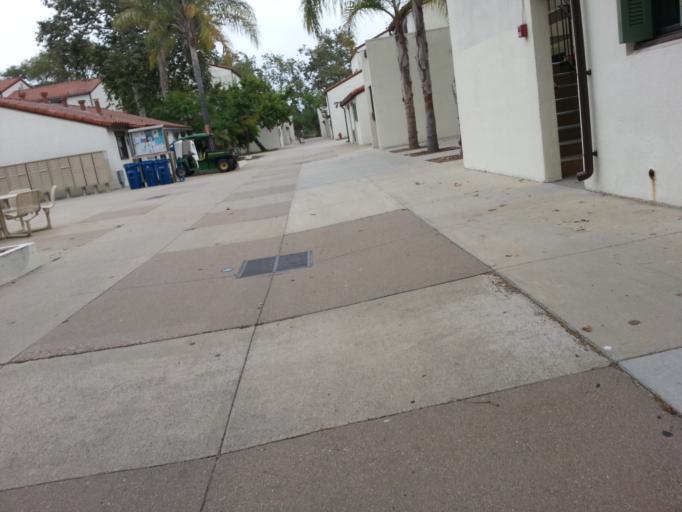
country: US
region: California
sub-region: Santa Barbara County
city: Isla Vista
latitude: 34.4227
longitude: -119.8632
